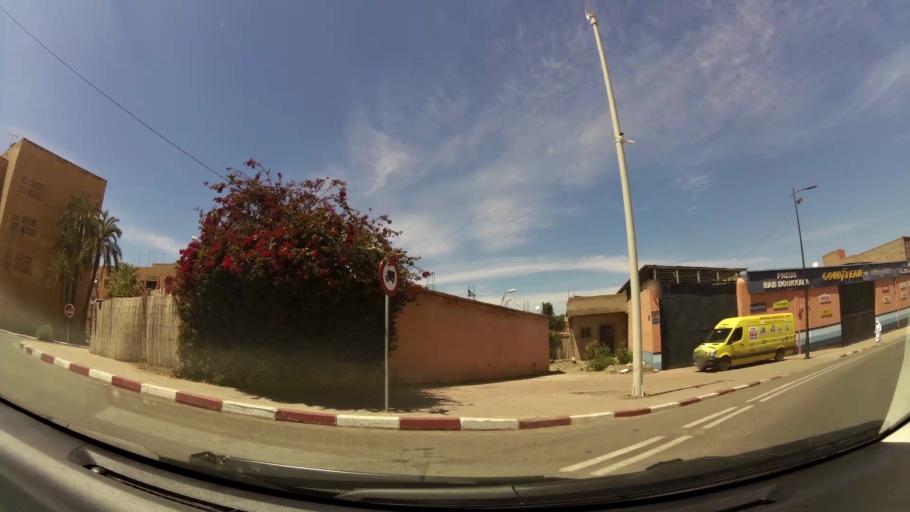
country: MA
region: Marrakech-Tensift-Al Haouz
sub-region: Marrakech
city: Marrakesh
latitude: 31.6311
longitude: -8.0009
